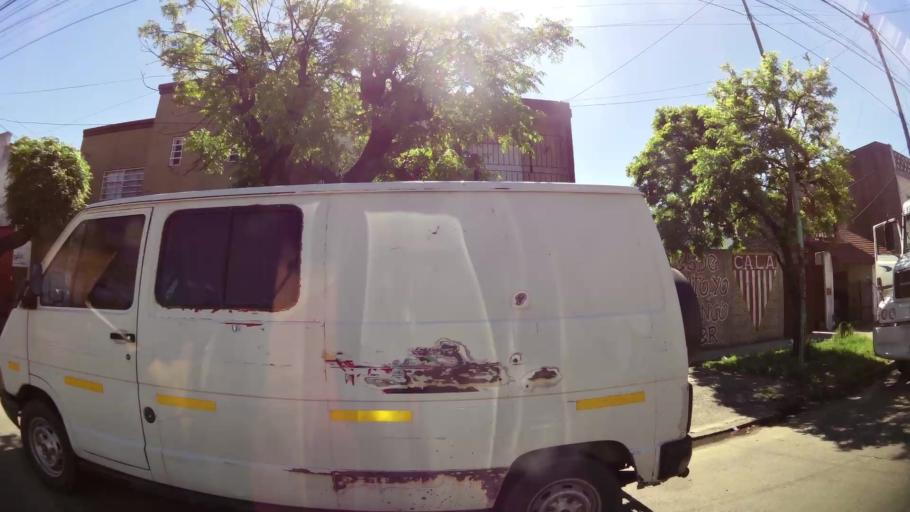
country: AR
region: Buenos Aires
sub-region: Partido de Lomas de Zamora
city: Lomas de Zamora
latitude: -34.7562
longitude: -58.4213
